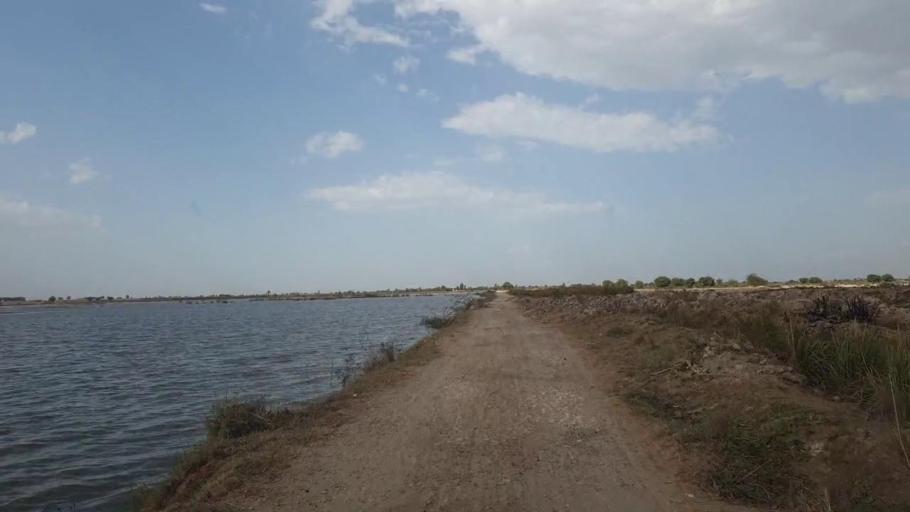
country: PK
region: Sindh
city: Shahdadpur
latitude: 25.9937
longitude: 68.4644
